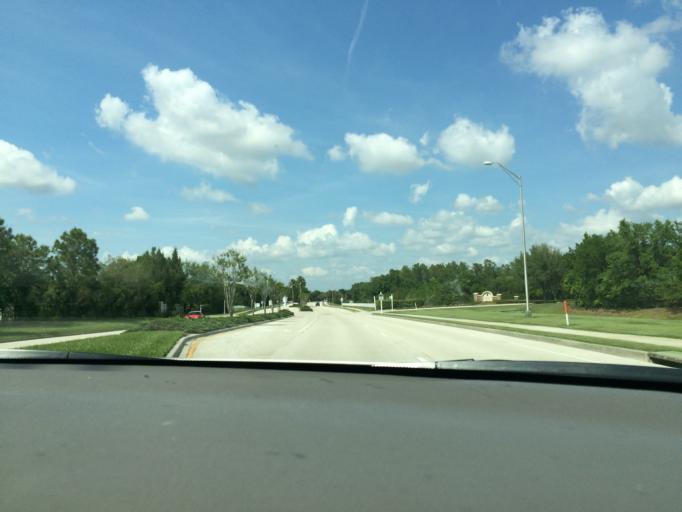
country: US
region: Florida
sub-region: Sarasota County
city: The Meadows
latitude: 27.4144
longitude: -82.3993
